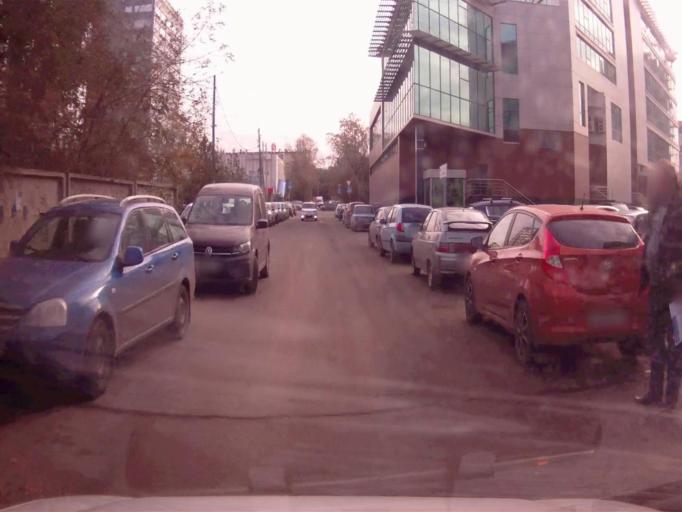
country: RU
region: Chelyabinsk
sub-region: Gorod Chelyabinsk
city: Chelyabinsk
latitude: 55.1709
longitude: 61.4142
